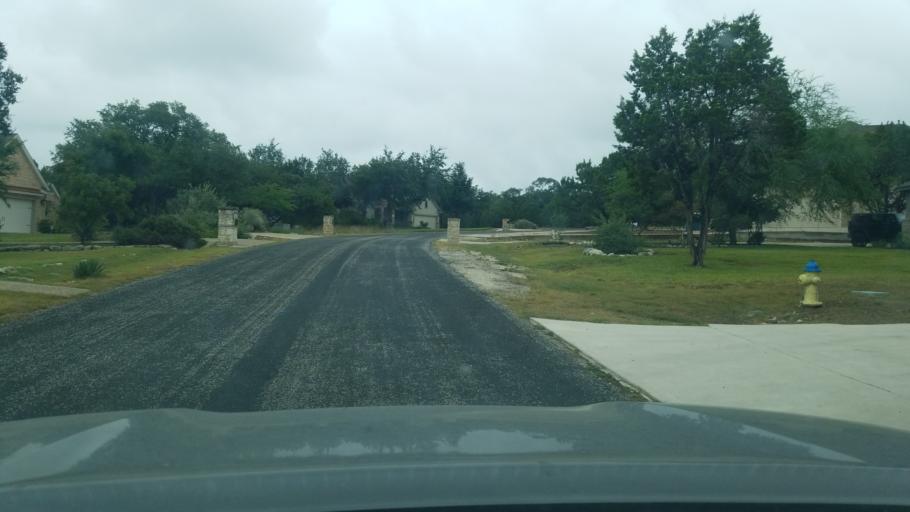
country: US
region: Texas
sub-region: Bexar County
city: Timberwood Park
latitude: 29.6988
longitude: -98.5085
